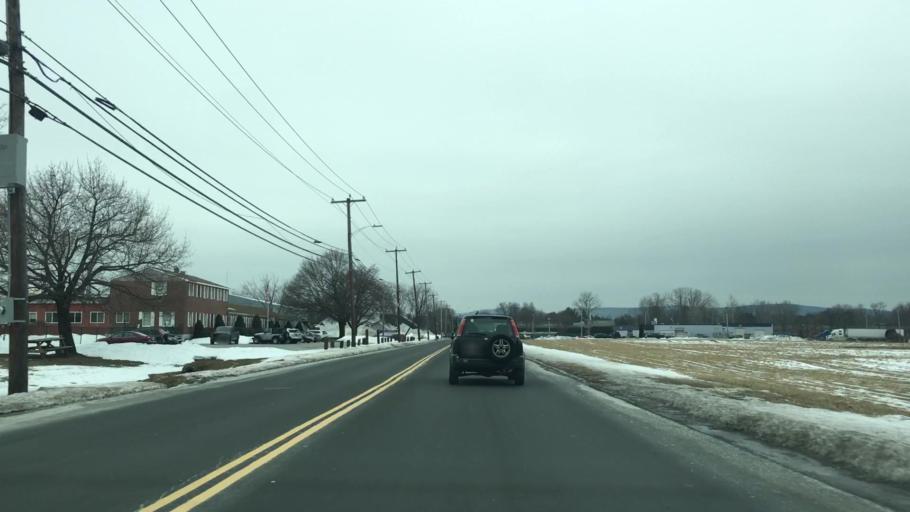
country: US
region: Massachusetts
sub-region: Hampden County
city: Westfield
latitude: 42.1255
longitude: -72.7239
